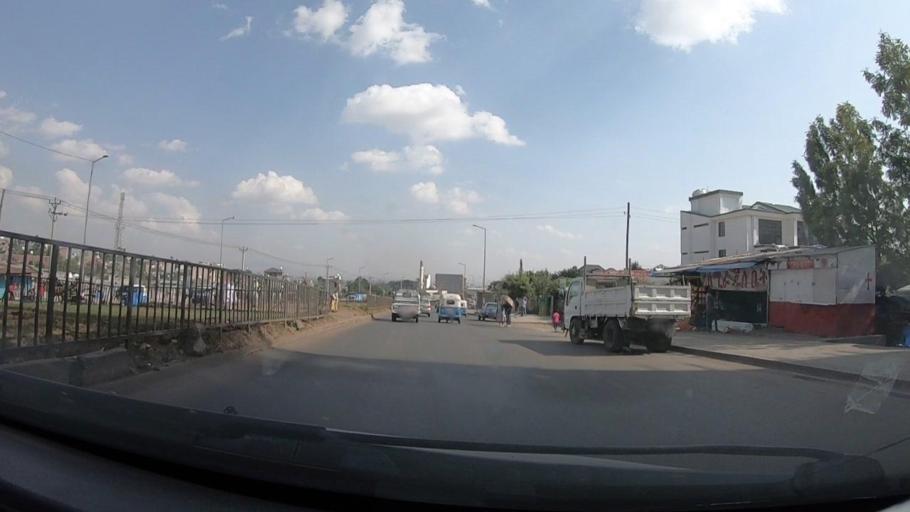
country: ET
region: Adis Abeba
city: Addis Ababa
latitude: 8.9911
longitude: 38.6899
